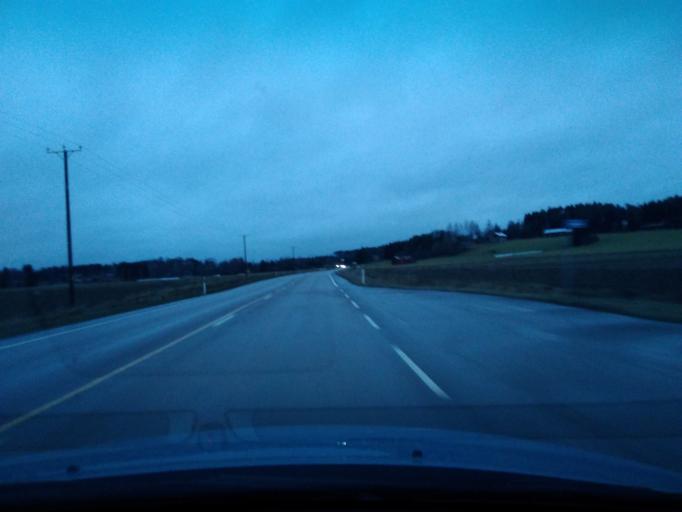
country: FI
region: Uusimaa
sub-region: Porvoo
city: Askola
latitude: 60.4535
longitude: 25.5829
